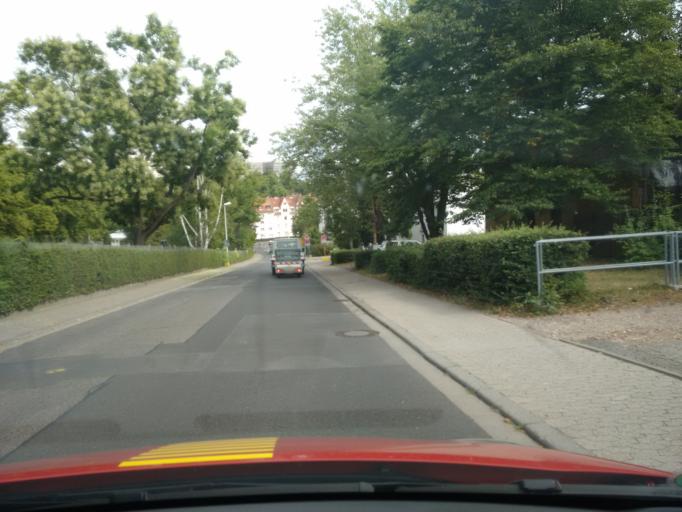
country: DE
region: Rheinland-Pfalz
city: Mainz
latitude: 49.9918
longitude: 8.2491
